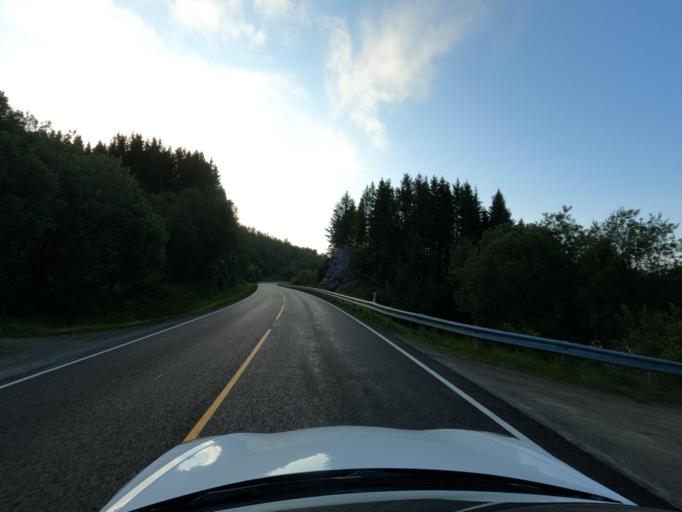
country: NO
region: Troms
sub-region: Skanland
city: Evenskjer
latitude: 68.6703
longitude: 16.5742
